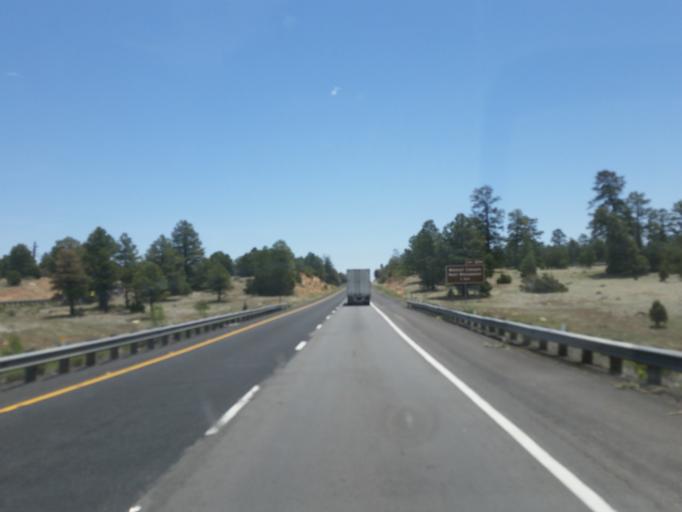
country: US
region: Arizona
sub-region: Coconino County
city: Flagstaff
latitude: 35.2142
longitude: -111.5424
